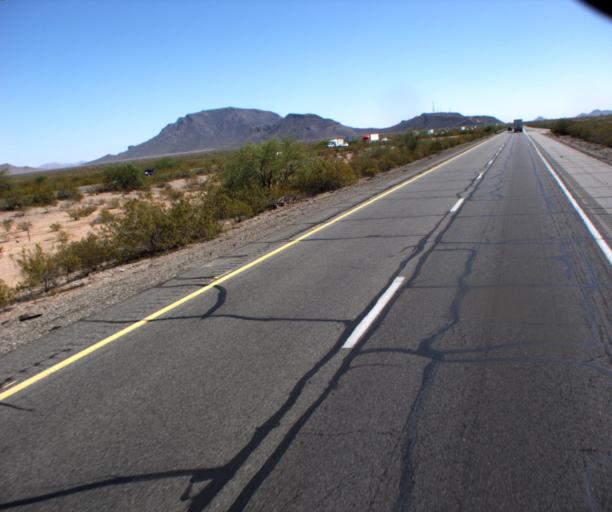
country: US
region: Arizona
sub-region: La Paz County
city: Salome
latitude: 33.5367
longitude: -113.1524
